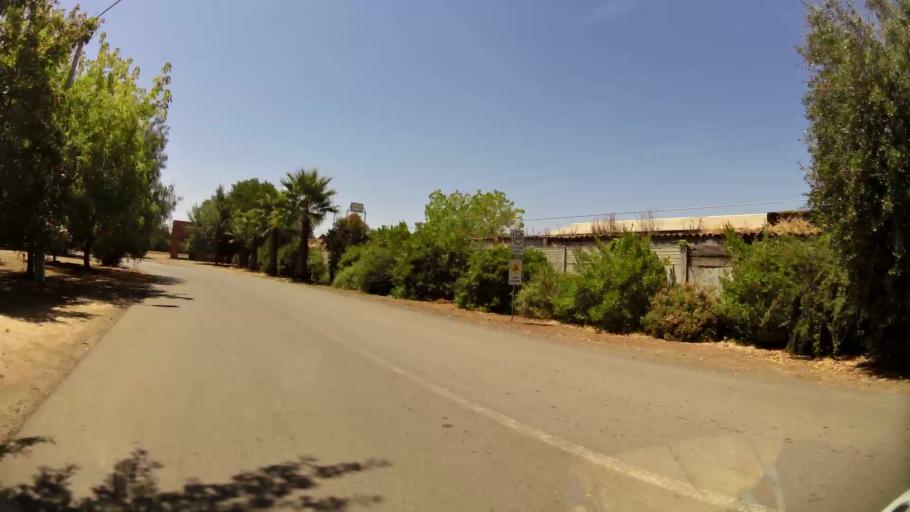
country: CL
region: Maule
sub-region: Provincia de Curico
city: Curico
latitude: -34.9947
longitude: -71.2049
